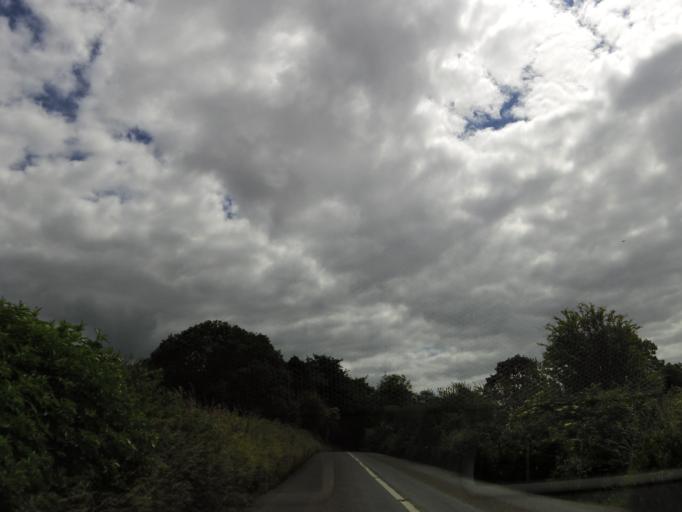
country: IE
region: Munster
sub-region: North Tipperary
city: Nenagh
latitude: 52.7931
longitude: -8.0406
